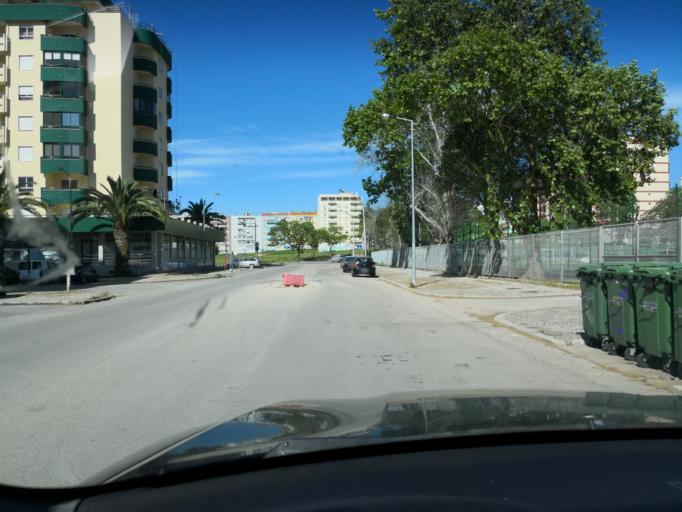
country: PT
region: Setubal
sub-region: Setubal
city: Setubal
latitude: 38.5365
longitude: -8.8894
